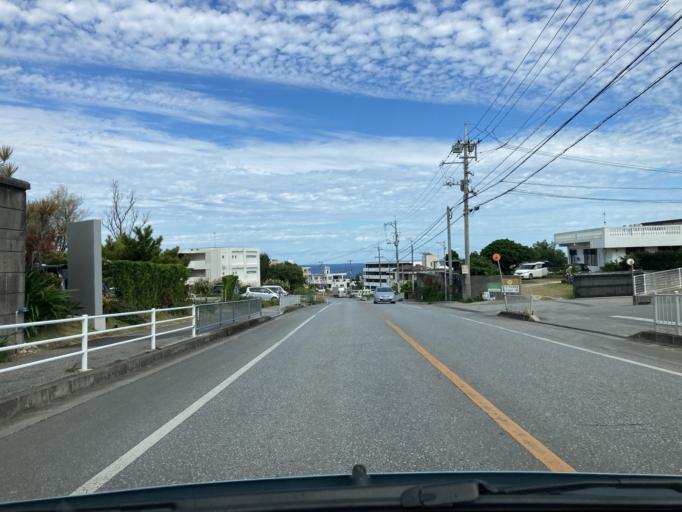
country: JP
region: Okinawa
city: Ishikawa
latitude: 26.4180
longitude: 127.7324
